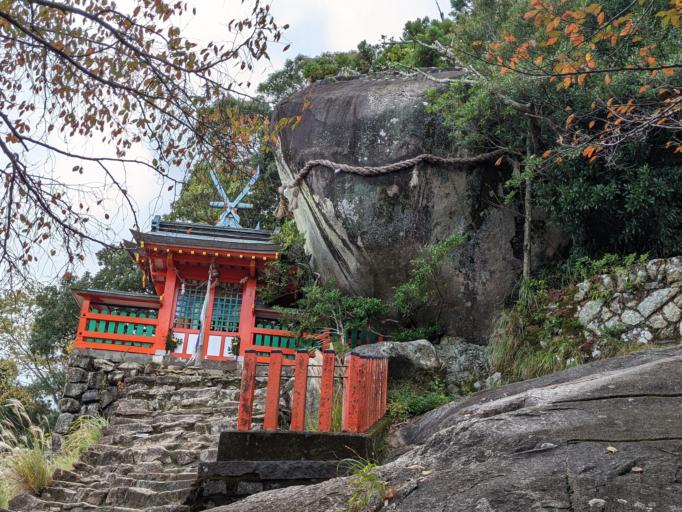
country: JP
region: Wakayama
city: Shingu
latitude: 33.7223
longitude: 135.9828
